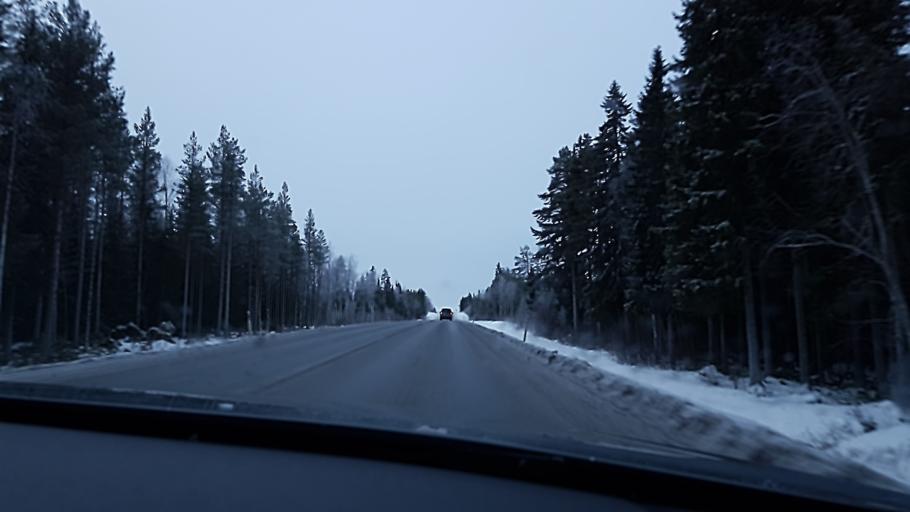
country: SE
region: Jaemtland
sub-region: OEstersunds Kommun
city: Ostersund
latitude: 63.2210
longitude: 14.7377
